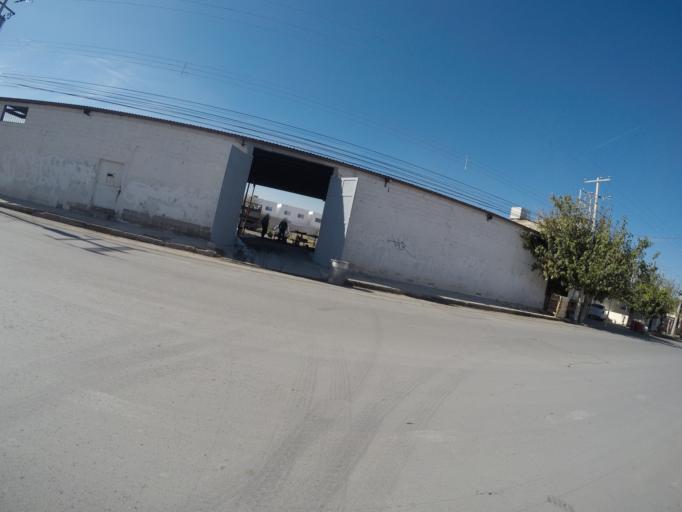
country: MX
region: Chihuahua
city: Ciudad Juarez
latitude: 31.7312
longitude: -106.4278
